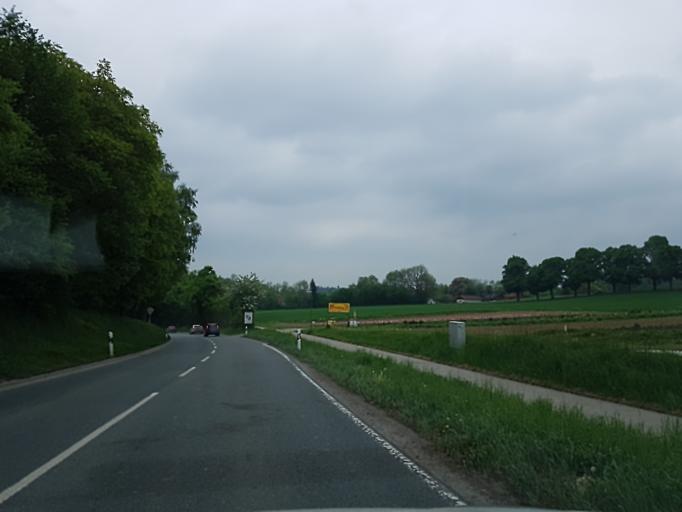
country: DE
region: Bavaria
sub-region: Upper Bavaria
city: Ebersberg
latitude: 48.0875
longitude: 11.9661
